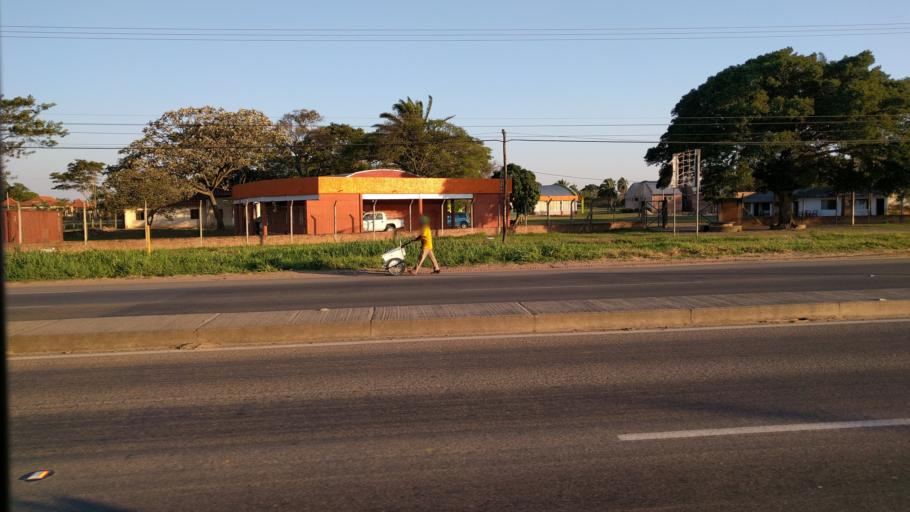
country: BO
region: Santa Cruz
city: Cotoca
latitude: -17.7663
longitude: -63.0468
